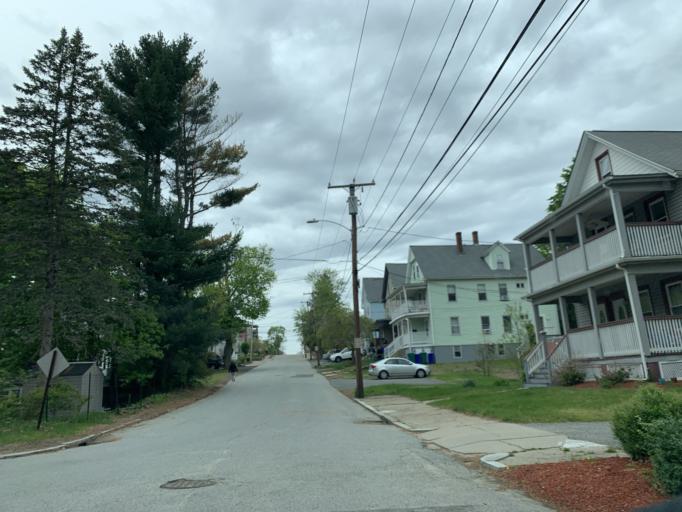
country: US
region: Massachusetts
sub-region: Bristol County
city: Attleboro
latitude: 41.9400
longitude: -71.2886
